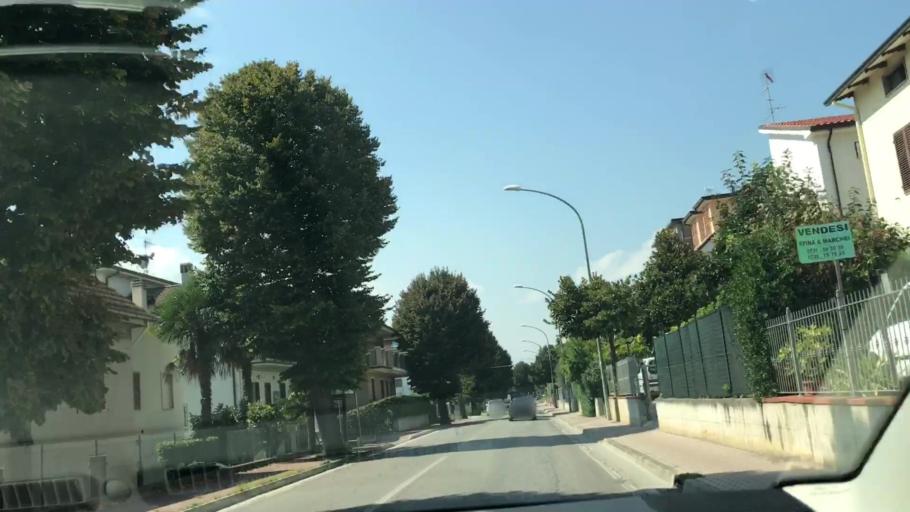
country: IT
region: The Marches
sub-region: Provincia di Ascoli Piceno
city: San Benedetto del Tronto
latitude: 42.9076
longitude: 13.8751
